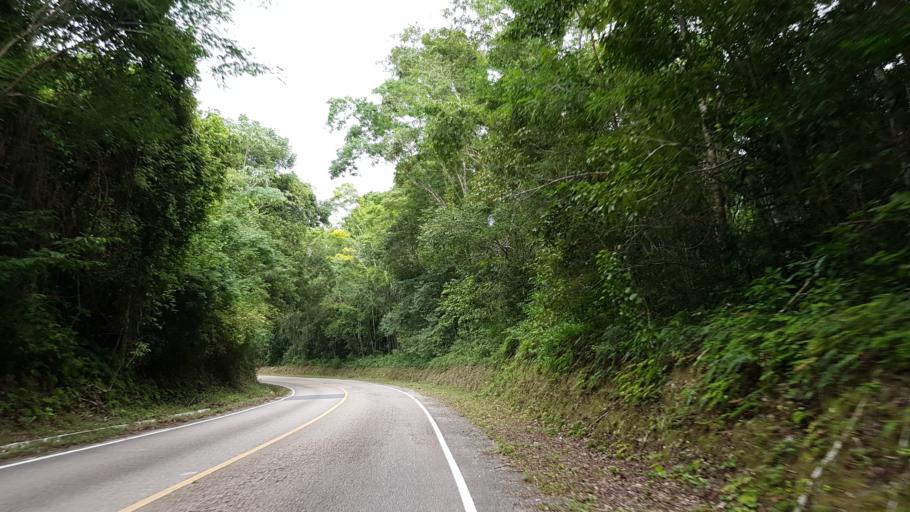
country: GT
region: Peten
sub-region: Municipio de San Jose
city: San Jose
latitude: 17.2101
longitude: -89.6168
